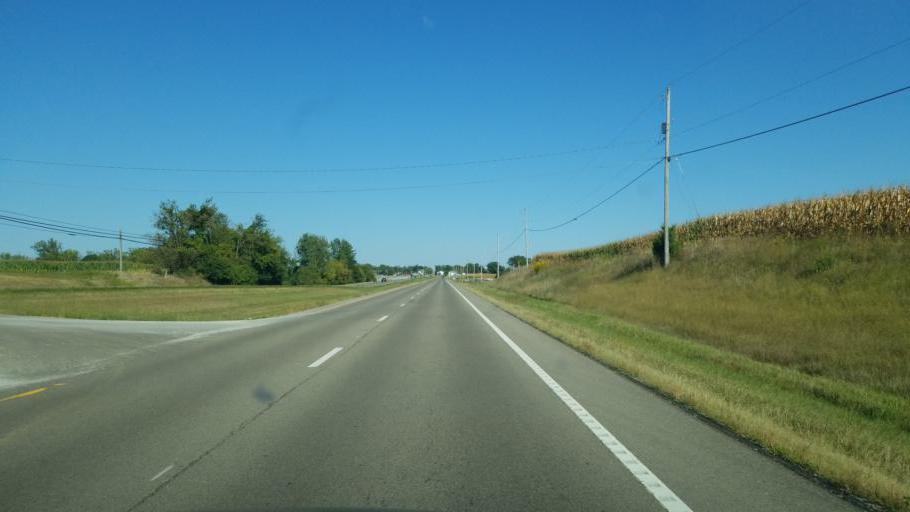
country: US
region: Ohio
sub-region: Clark County
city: Lisbon
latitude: 39.9268
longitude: -83.6315
